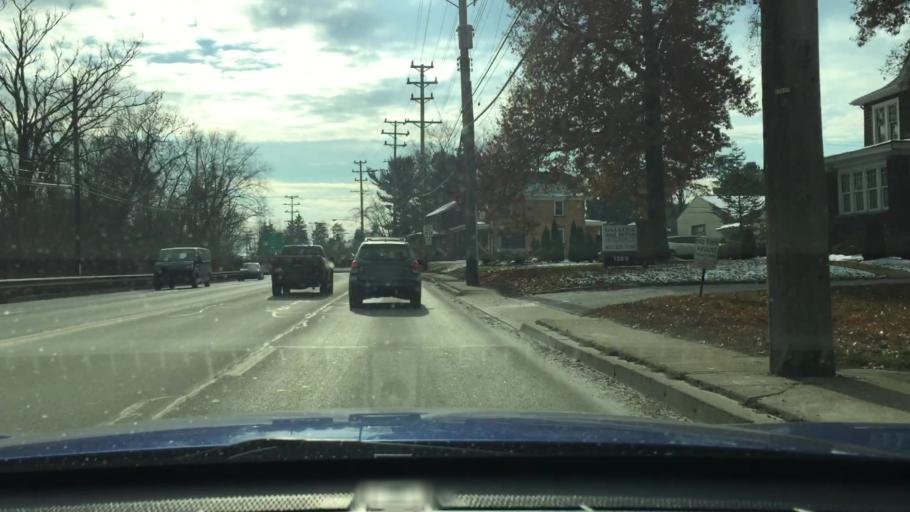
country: US
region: Pennsylvania
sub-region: Allegheny County
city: Heidelberg
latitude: 40.3751
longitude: -80.0986
